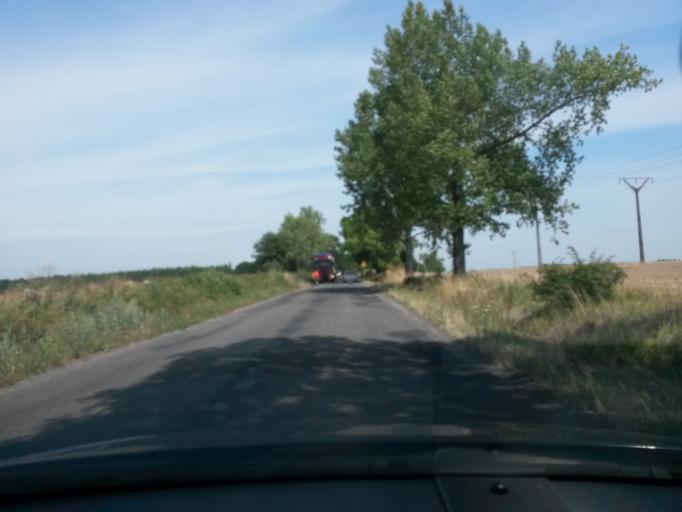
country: PL
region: Lower Silesian Voivodeship
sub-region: Powiat legnicki
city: Prochowice
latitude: 51.2289
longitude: 16.3593
